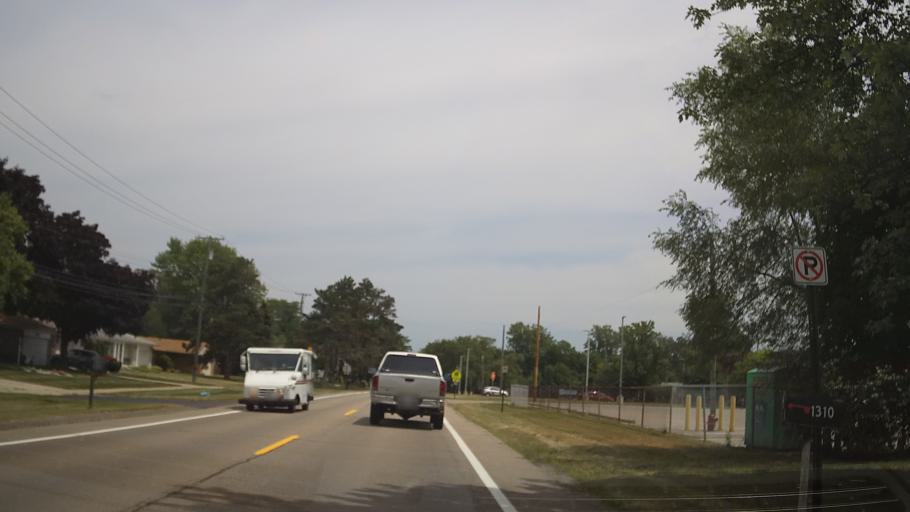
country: US
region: Michigan
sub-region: Oakland County
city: Troy
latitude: 42.6071
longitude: -83.1240
